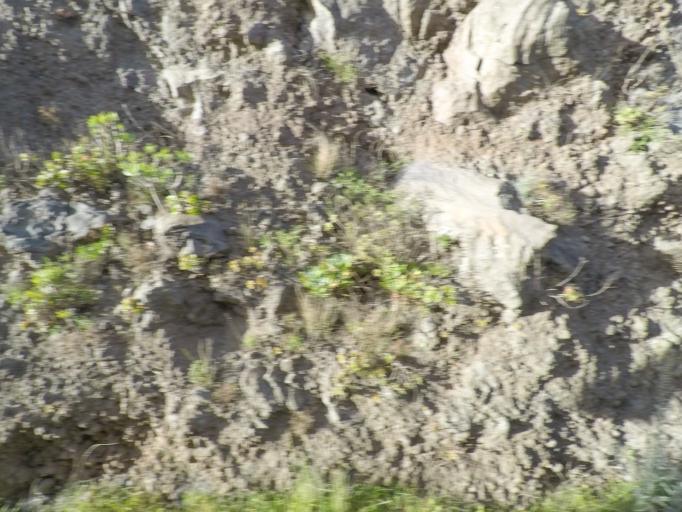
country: ES
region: Canary Islands
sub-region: Provincia de Santa Cruz de Tenerife
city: San Sebastian de la Gomera
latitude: 28.0985
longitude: -17.1807
